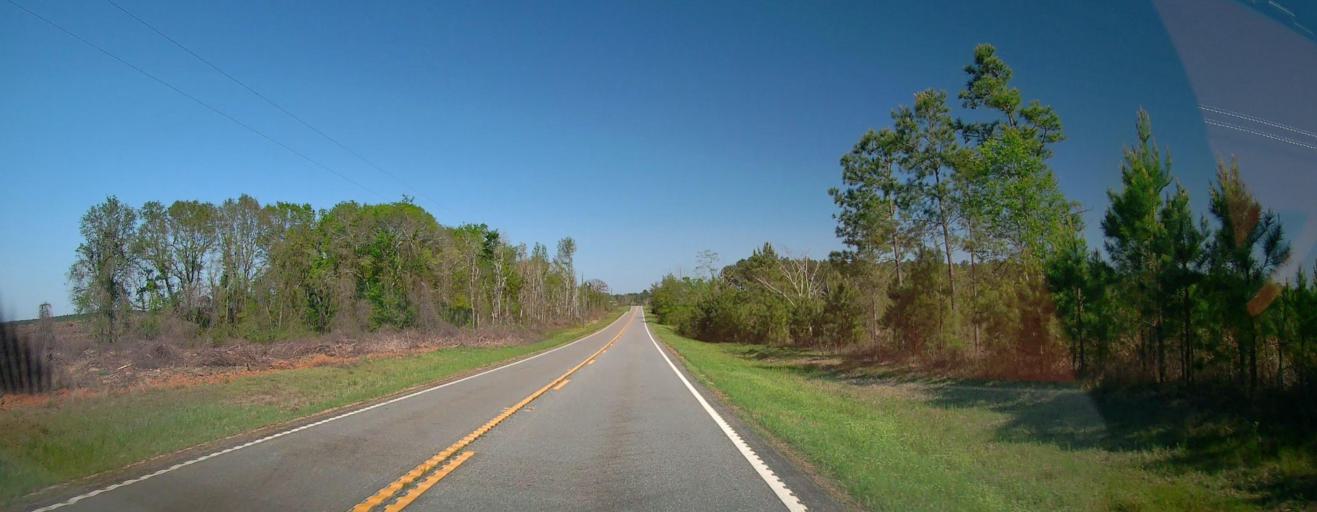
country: US
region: Georgia
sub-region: Dooly County
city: Unadilla
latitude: 32.2540
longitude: -83.6293
